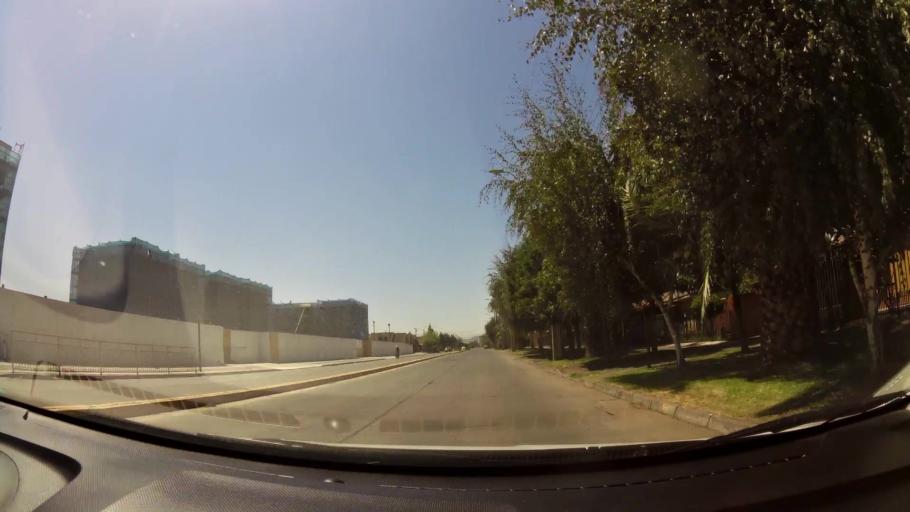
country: CL
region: Maule
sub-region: Provincia de Curico
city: Curico
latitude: -34.9713
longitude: -71.2243
